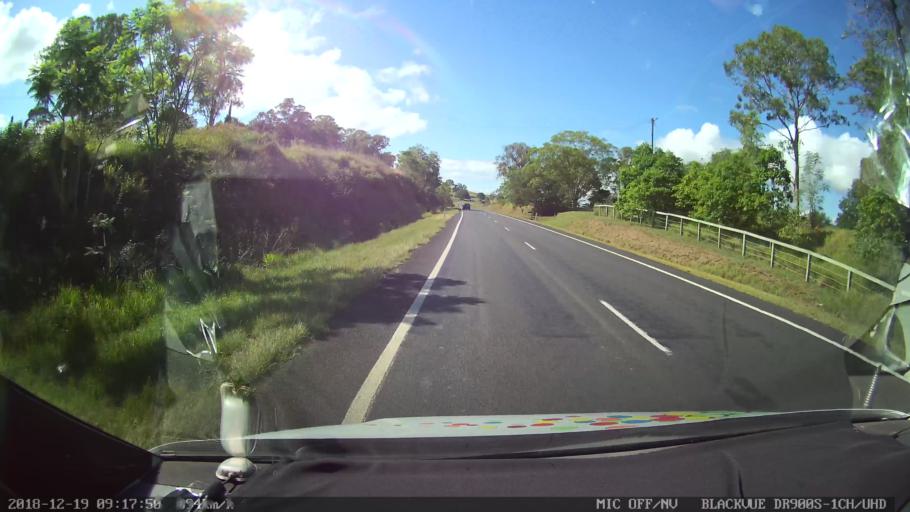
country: AU
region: New South Wales
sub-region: Kyogle
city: Kyogle
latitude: -28.5392
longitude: 152.9755
